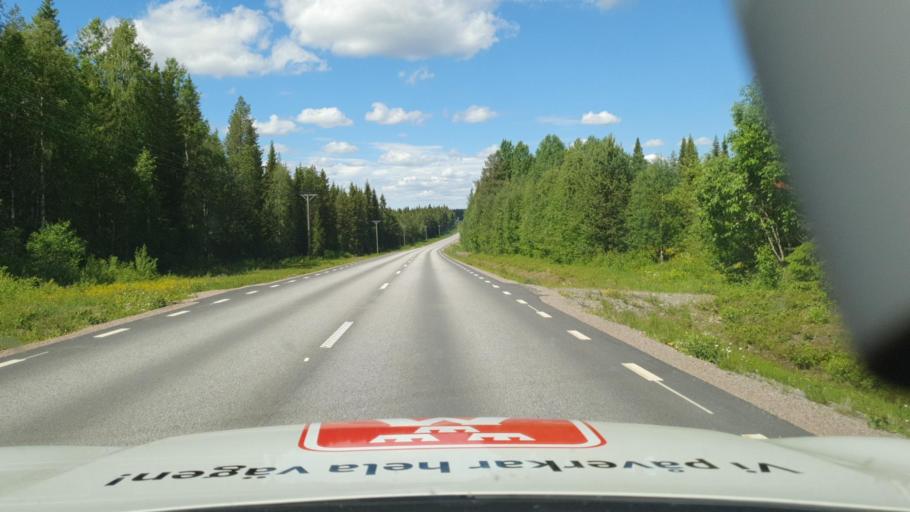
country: SE
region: Vaesterbotten
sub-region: Skelleftea Kommun
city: Boliden
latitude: 64.9203
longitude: 20.3299
